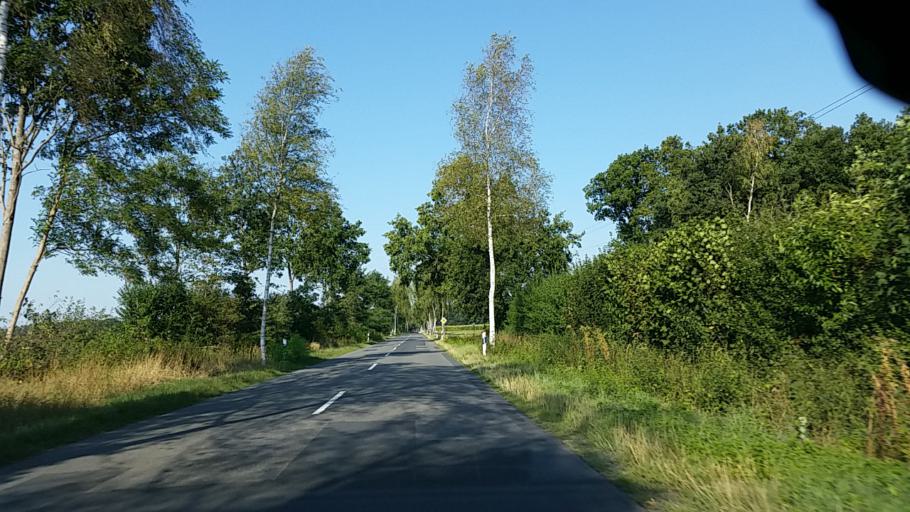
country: DE
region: Lower Saxony
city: Barwedel
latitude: 52.5280
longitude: 10.7559
